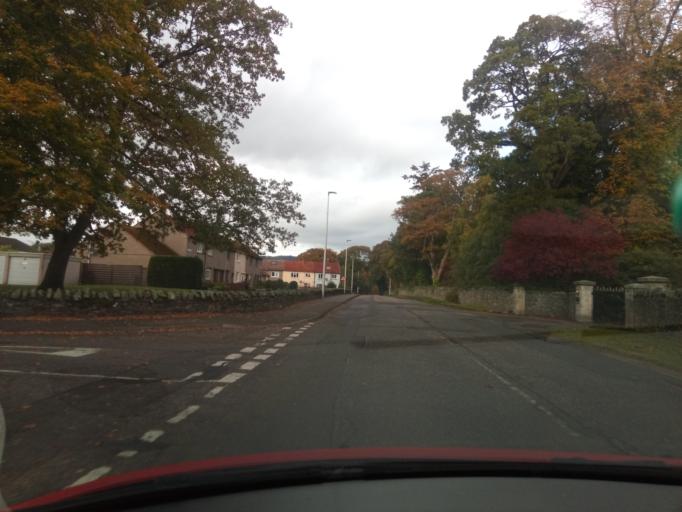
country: GB
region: Scotland
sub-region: The Scottish Borders
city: Peebles
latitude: 55.6468
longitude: -3.1798
